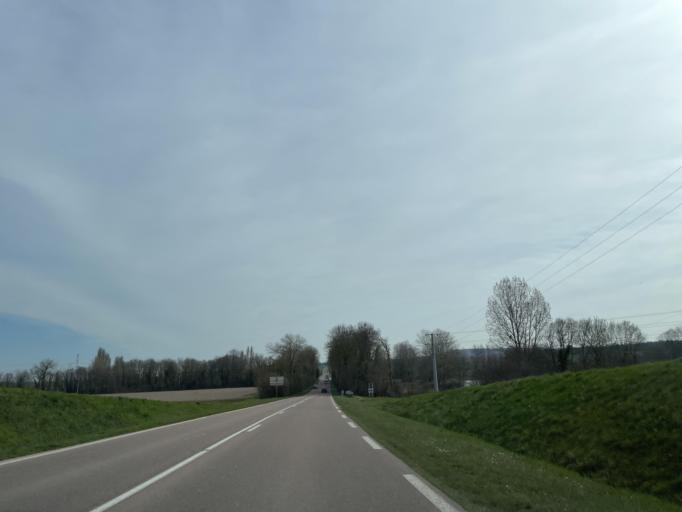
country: FR
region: Champagne-Ardenne
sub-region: Departement de l'Aube
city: Nogent-sur-Seine
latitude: 48.4951
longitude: 3.5274
